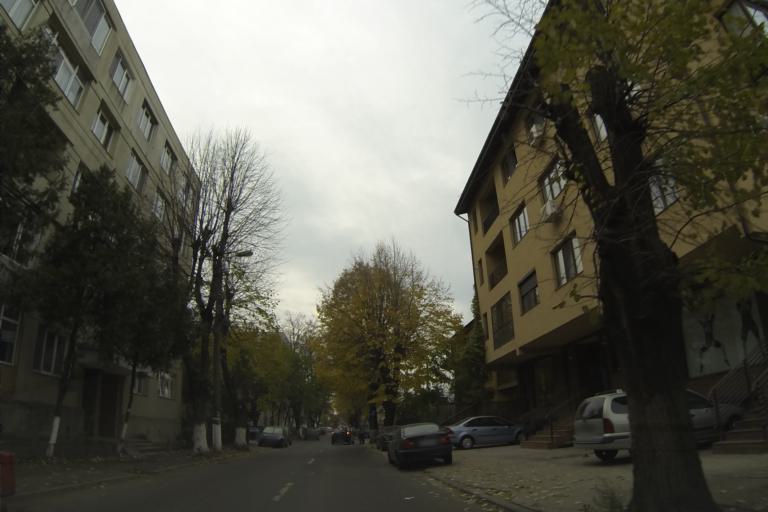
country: RO
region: Ilfov
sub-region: Comuna Chiajna
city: Rosu
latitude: 44.4356
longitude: 26.0111
